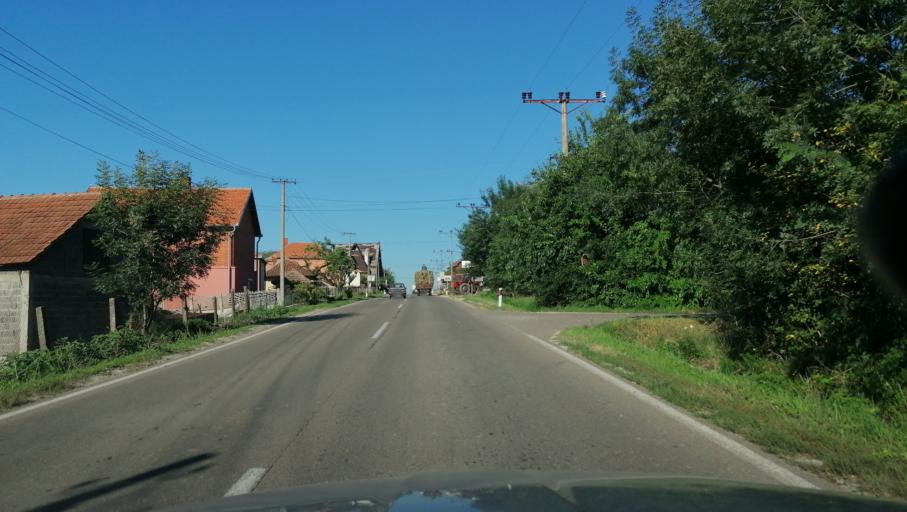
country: RS
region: Central Serbia
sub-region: Sumadijski Okrug
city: Knic
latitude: 43.9003
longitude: 20.6254
